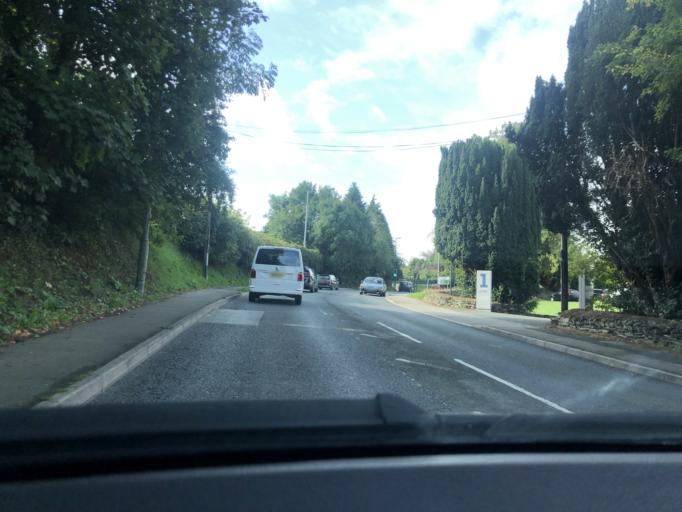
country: GB
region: England
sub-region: Cornwall
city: Launceston
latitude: 50.6312
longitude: -4.3662
